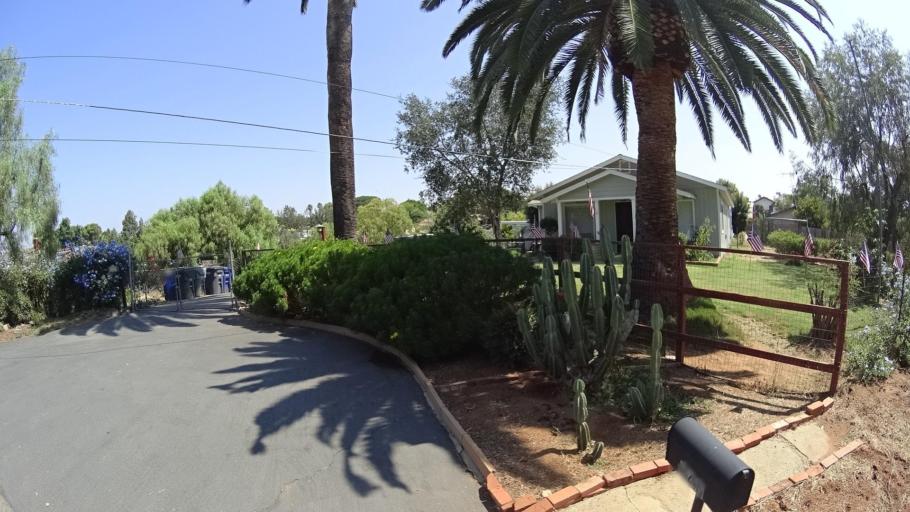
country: US
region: California
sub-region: San Diego County
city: Vista
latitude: 33.2433
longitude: -117.2381
